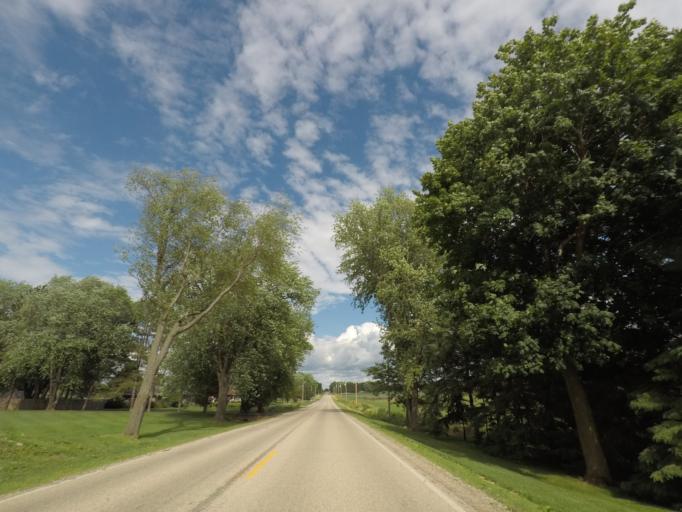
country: US
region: Wisconsin
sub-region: Rock County
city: Janesville
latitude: 42.7011
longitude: -89.0792
